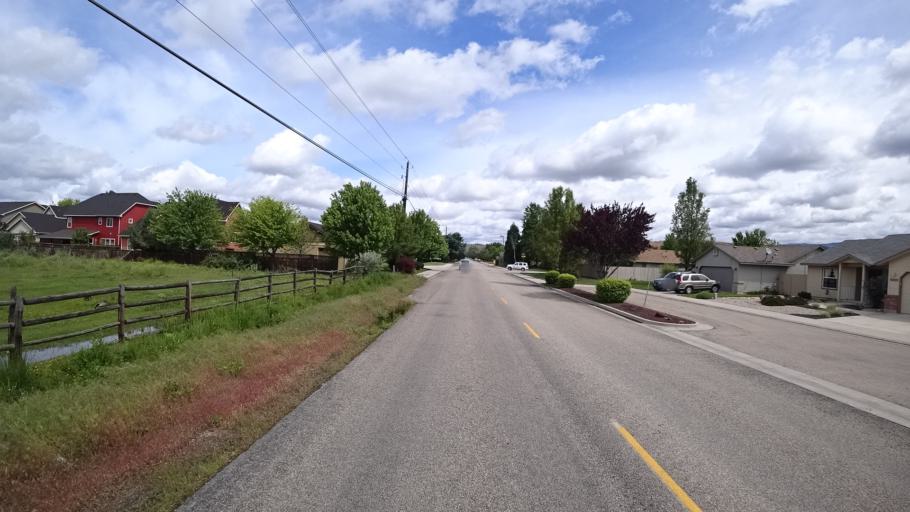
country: US
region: Idaho
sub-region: Ada County
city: Eagle
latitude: 43.6802
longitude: -116.3016
